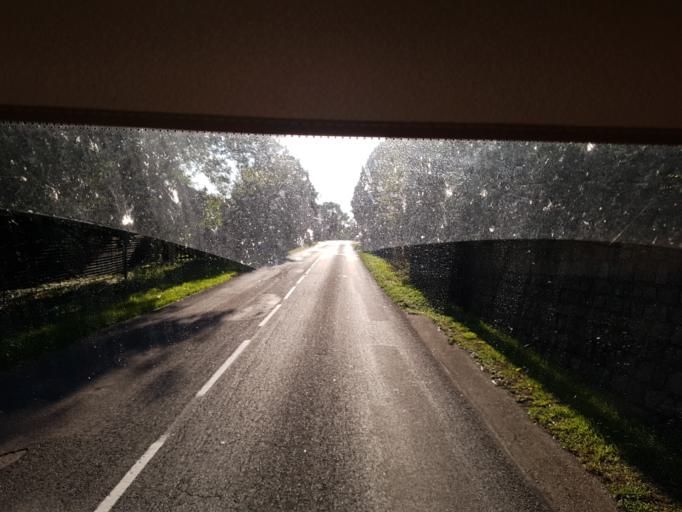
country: FR
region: Rhone-Alpes
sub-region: Departement de l'Ain
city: Priay
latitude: 46.0295
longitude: 5.3012
